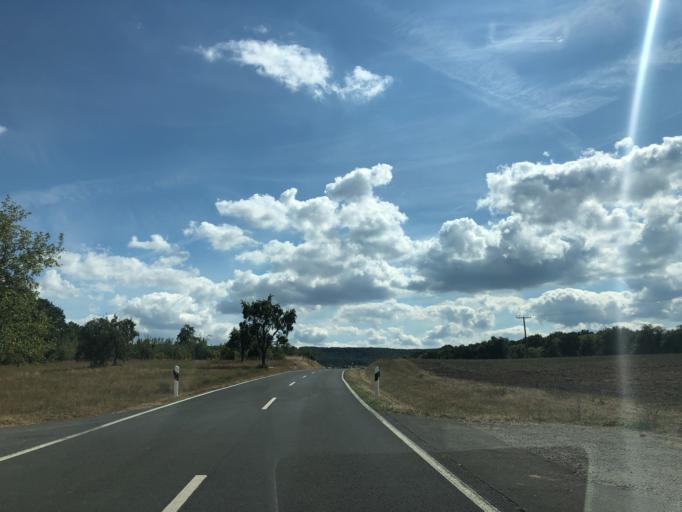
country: DE
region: Bavaria
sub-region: Regierungsbezirk Unterfranken
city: Oberschwarzach
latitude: 49.8439
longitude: 10.4303
